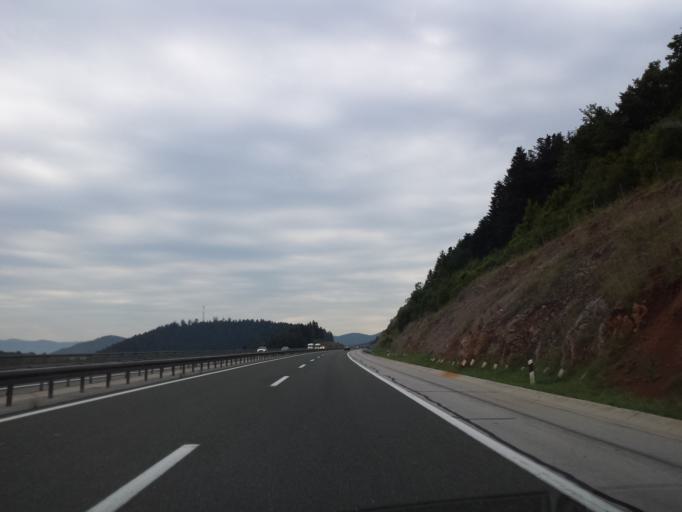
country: HR
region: Licko-Senjska
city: Otocac
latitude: 44.8552
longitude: 15.2232
